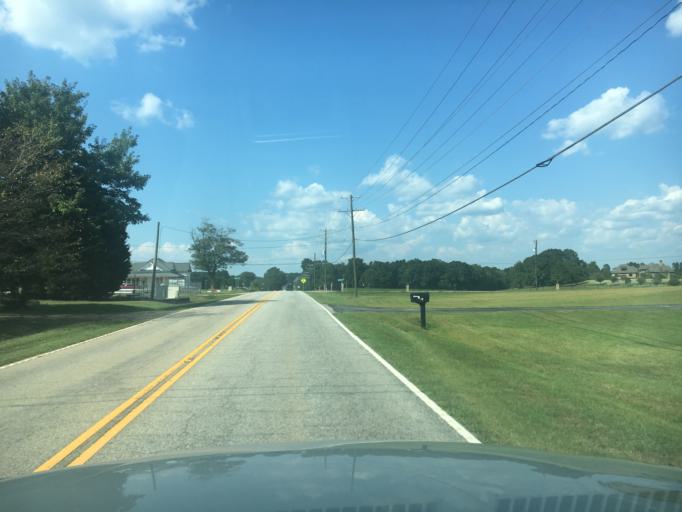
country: US
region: South Carolina
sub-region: Anderson County
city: Pendleton
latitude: 34.5702
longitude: -82.8074
